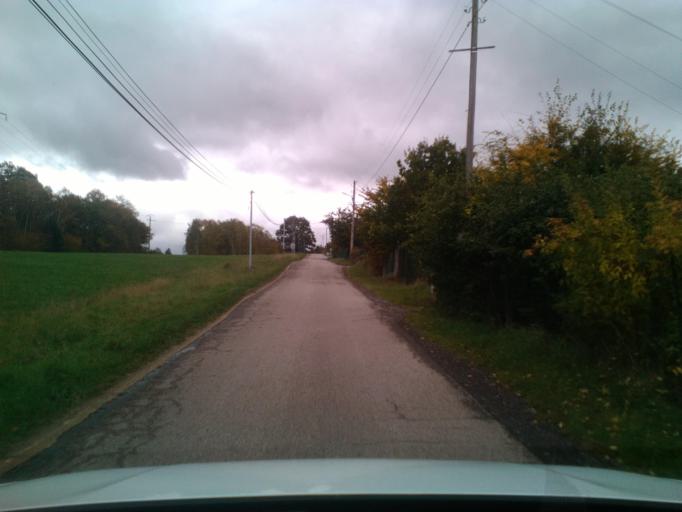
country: FR
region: Lorraine
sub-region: Departement des Vosges
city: Moyenmoutier
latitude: 48.3720
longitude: 6.8869
